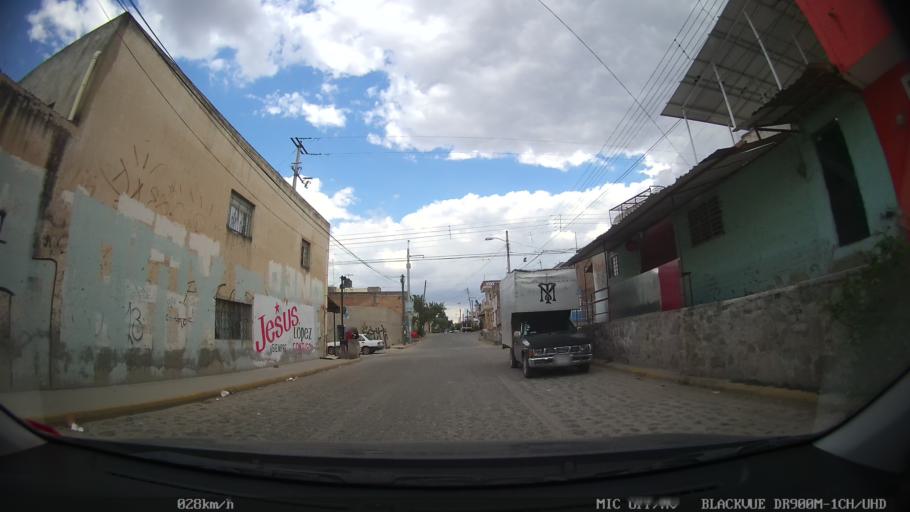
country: MX
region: Jalisco
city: Tonala
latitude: 20.6569
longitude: -103.2551
